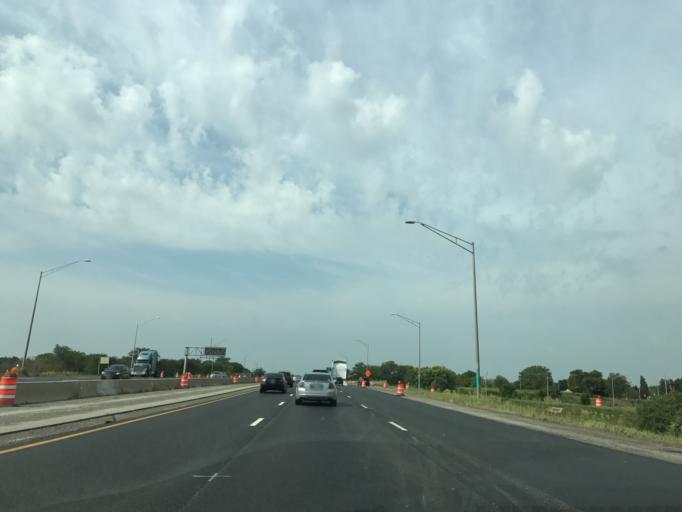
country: US
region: Illinois
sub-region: Cook County
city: Lemont
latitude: 41.7184
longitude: -88.0042
